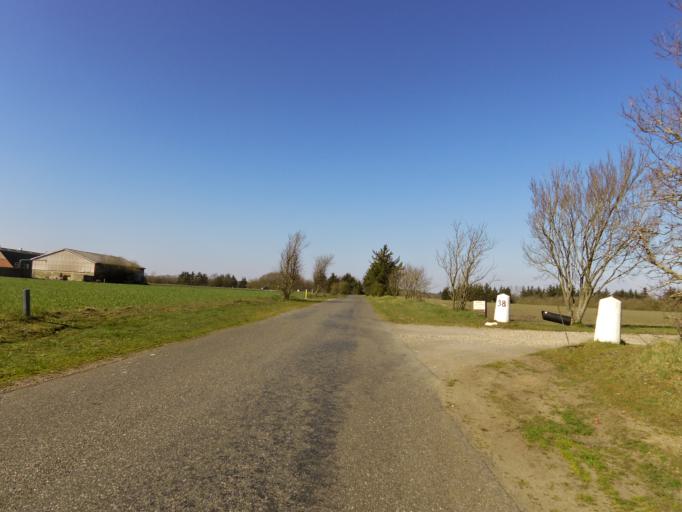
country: DK
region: South Denmark
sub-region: Esbjerg Kommune
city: Ribe
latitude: 55.3658
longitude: 8.8070
